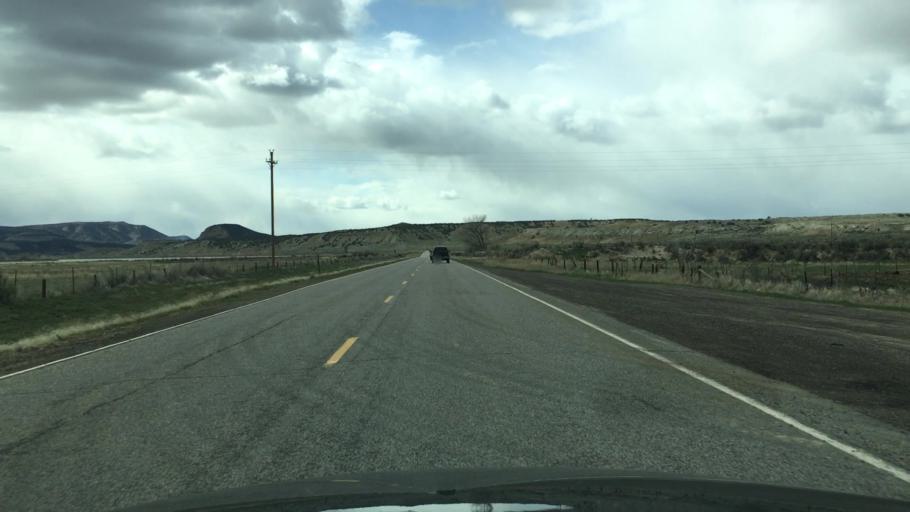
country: US
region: Colorado
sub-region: Rio Blanco County
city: Meeker
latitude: 40.0836
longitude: -108.1949
